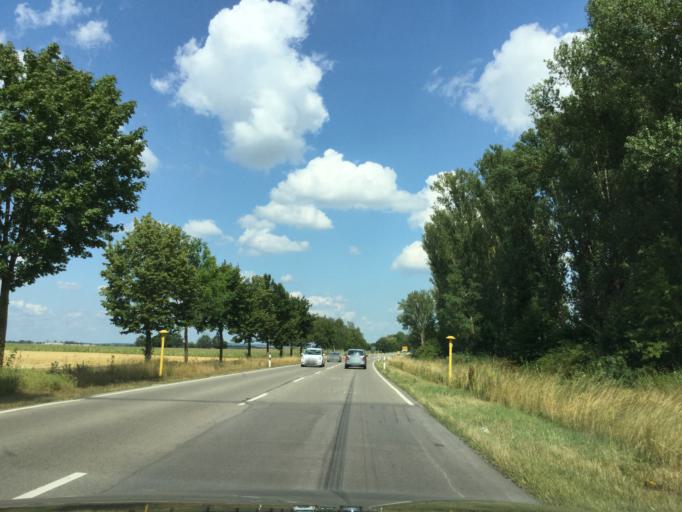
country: DE
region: Bavaria
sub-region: Regierungsbezirk Mittelfranken
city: Gallmersgarten
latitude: 49.4524
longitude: 10.2785
